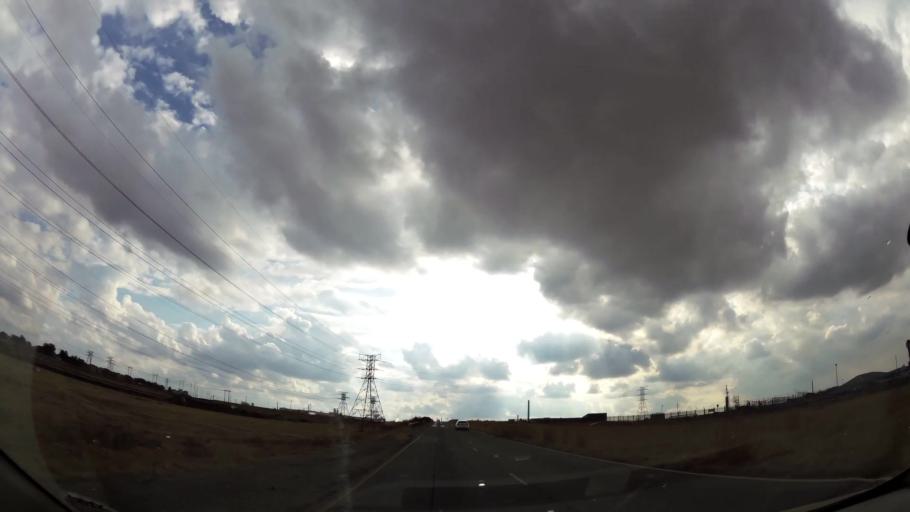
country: ZA
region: Orange Free State
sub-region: Fezile Dabi District Municipality
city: Sasolburg
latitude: -26.8348
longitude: 27.8651
